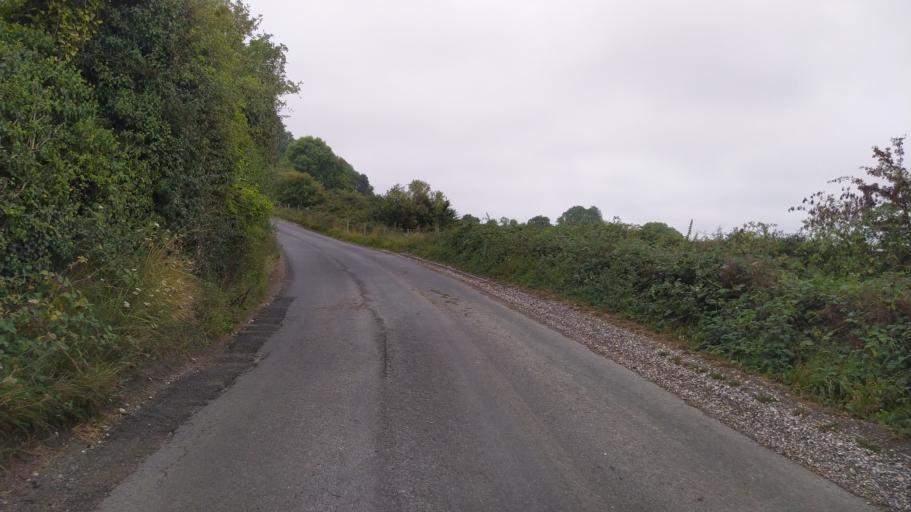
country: GB
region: England
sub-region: Wiltshire
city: Dinton
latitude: 51.0420
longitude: -1.9974
